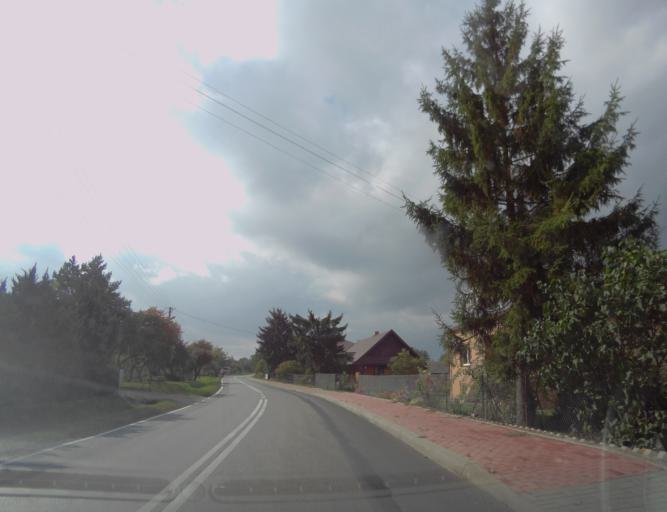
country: PL
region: Lublin Voivodeship
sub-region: Powiat krasnostawski
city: Gorzkow
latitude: 50.9381
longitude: 23.0007
